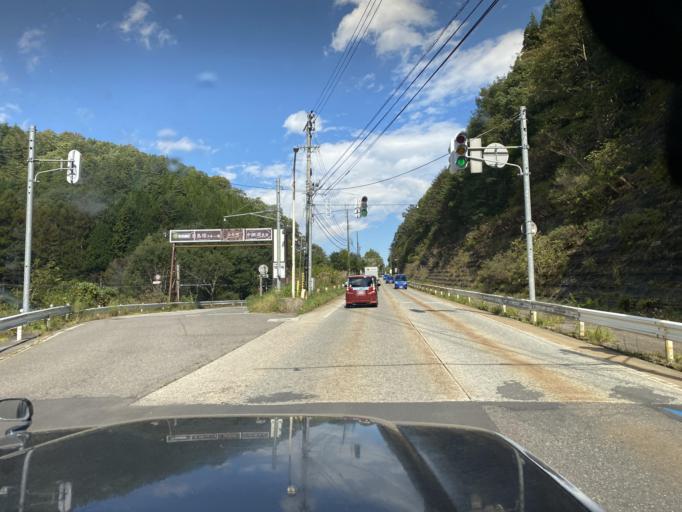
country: JP
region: Nagano
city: Omachi
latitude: 36.5889
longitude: 137.8419
